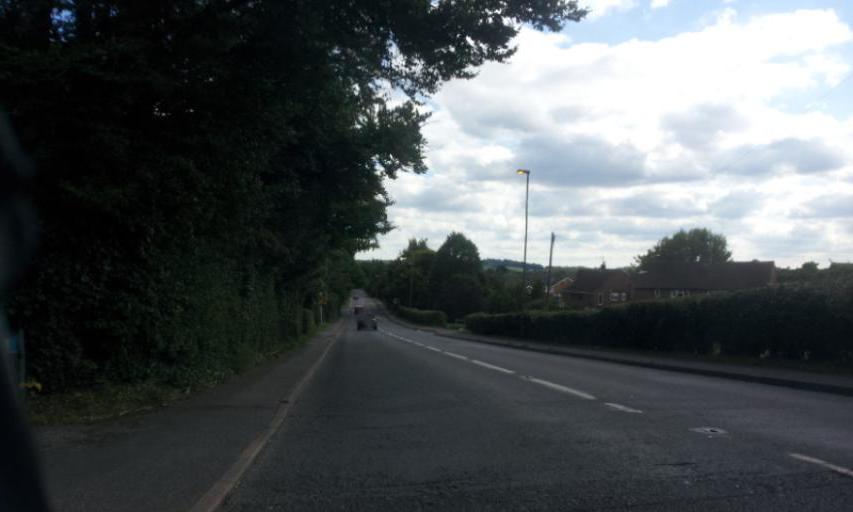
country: GB
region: England
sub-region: Kent
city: Staplehurst
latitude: 51.1576
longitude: 0.5525
